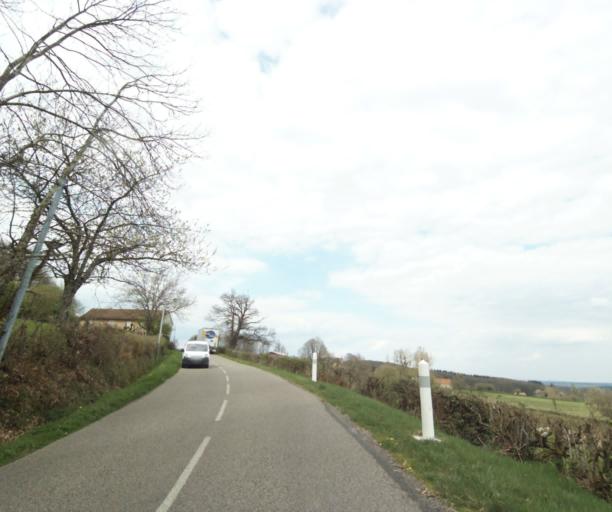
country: FR
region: Bourgogne
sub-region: Departement de Saone-et-Loire
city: Ciry-le-Noble
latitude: 46.5454
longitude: 4.3104
